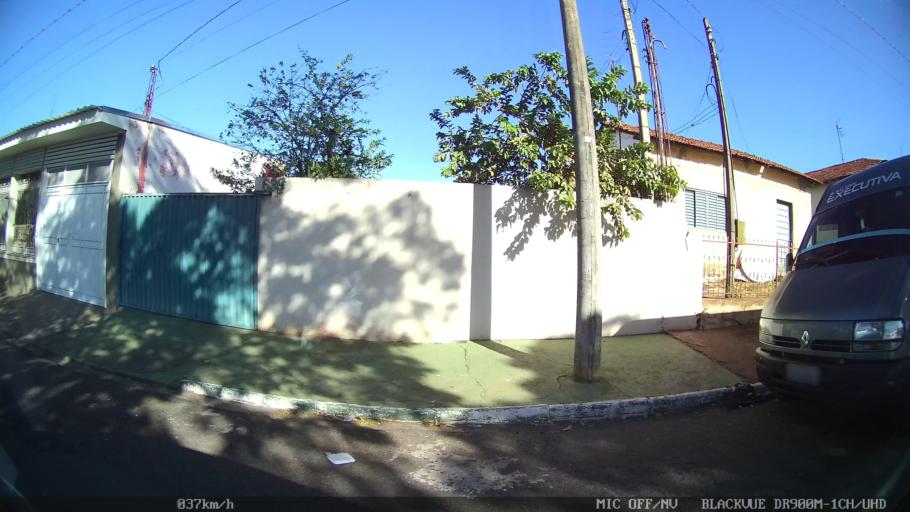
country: BR
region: Sao Paulo
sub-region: Olimpia
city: Olimpia
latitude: -20.7448
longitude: -48.9090
